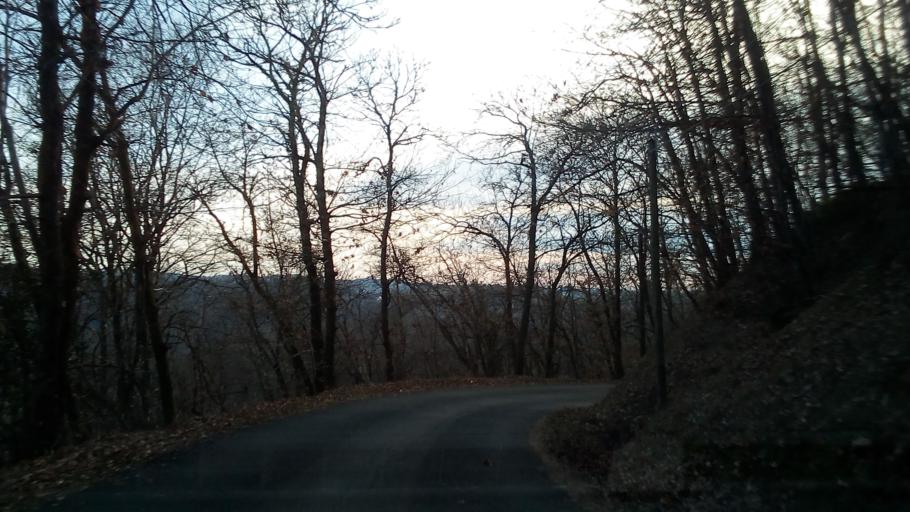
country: FR
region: Limousin
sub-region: Departement de la Correze
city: Naves
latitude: 45.3051
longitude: 1.7815
